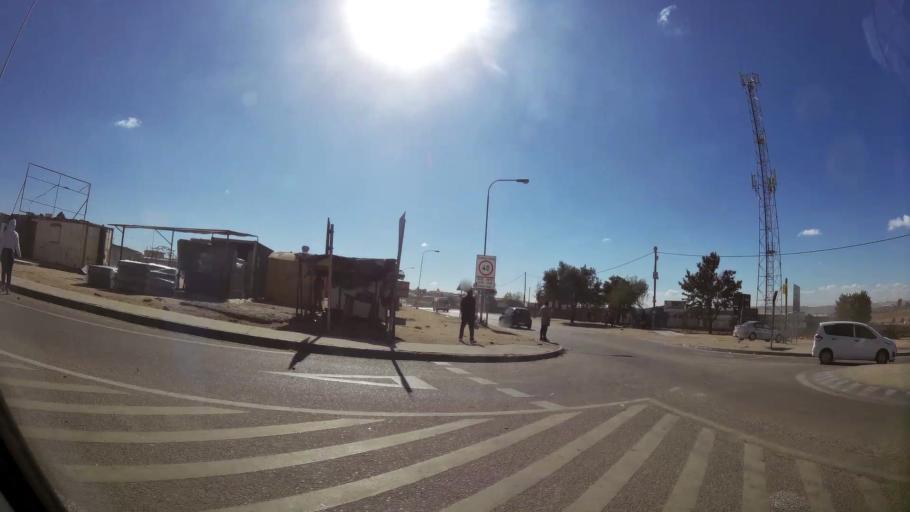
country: ZA
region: Gauteng
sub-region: City of Johannesburg Metropolitan Municipality
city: Midrand
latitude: -25.9167
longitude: 28.0952
